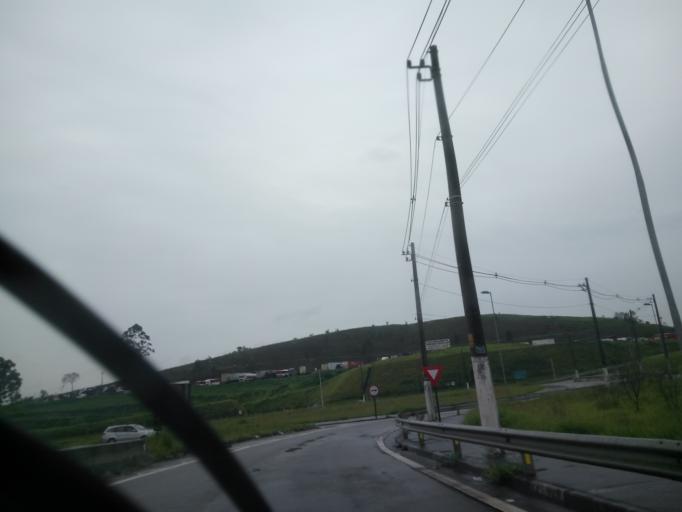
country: BR
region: Sao Paulo
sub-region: Sao Bernardo Do Campo
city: Sao Bernardo do Campo
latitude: -23.7577
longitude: -46.5917
